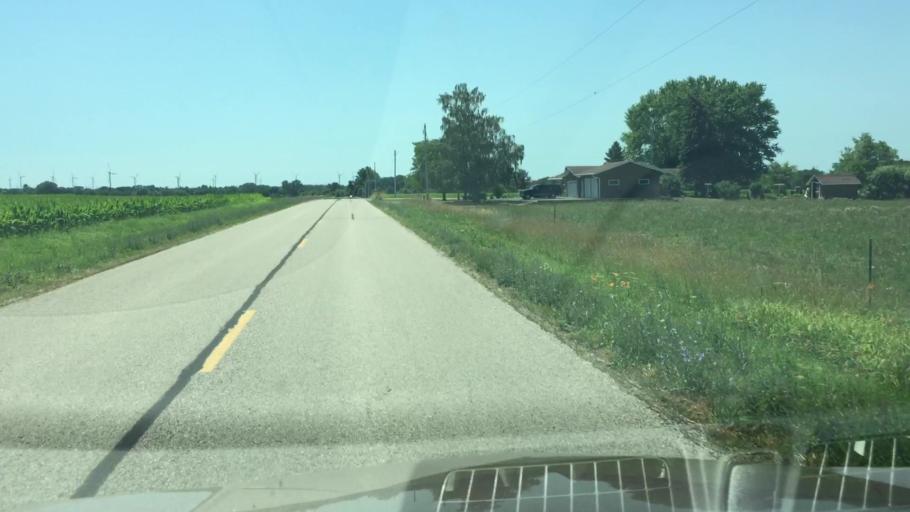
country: US
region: Wisconsin
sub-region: Fond du Lac County
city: Saint Peter
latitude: 43.9493
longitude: -88.3114
